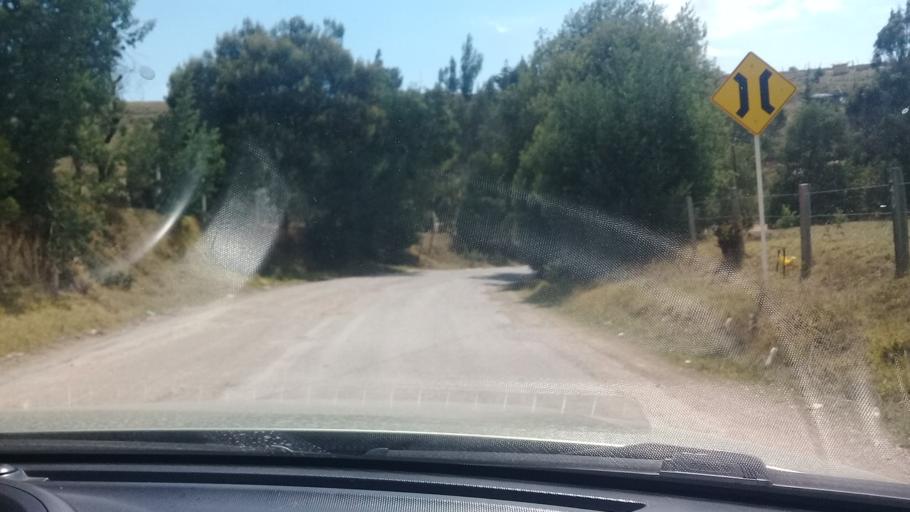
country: CO
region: Boyaca
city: Siachoque
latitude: 5.5515
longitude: -73.2885
